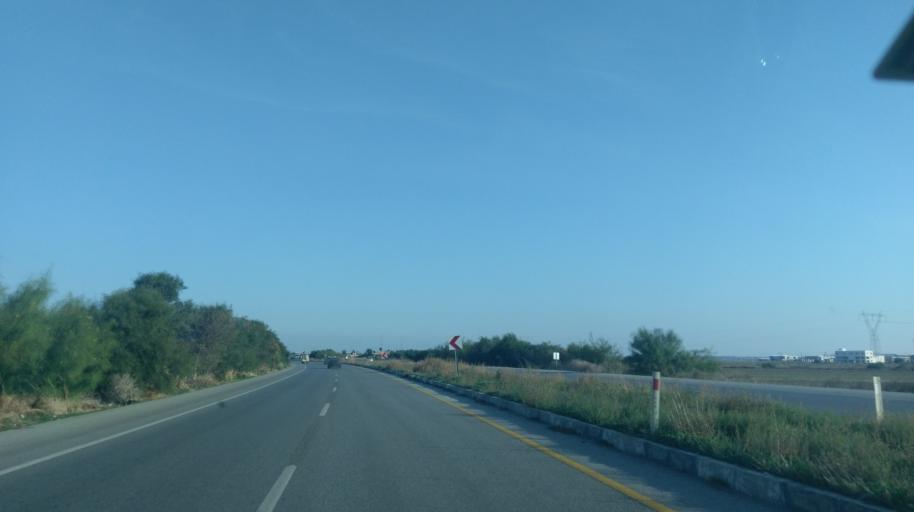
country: CY
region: Ammochostos
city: Acheritou
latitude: 35.1401
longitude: 33.8669
